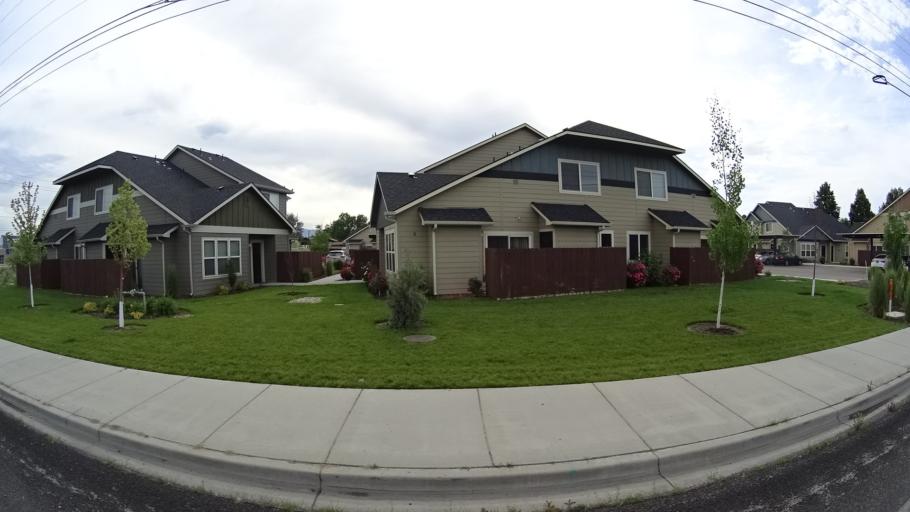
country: US
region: Idaho
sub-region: Ada County
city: Meridian
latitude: 43.6041
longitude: -116.3744
